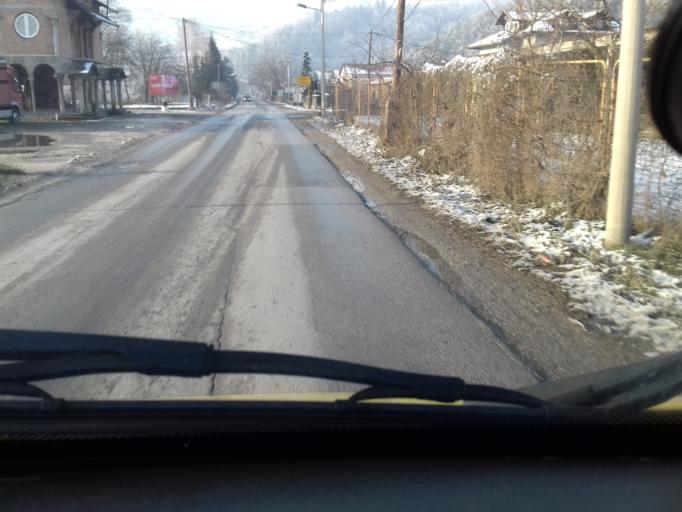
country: BA
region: Federation of Bosnia and Herzegovina
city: Mahala
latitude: 43.9952
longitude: 18.2208
